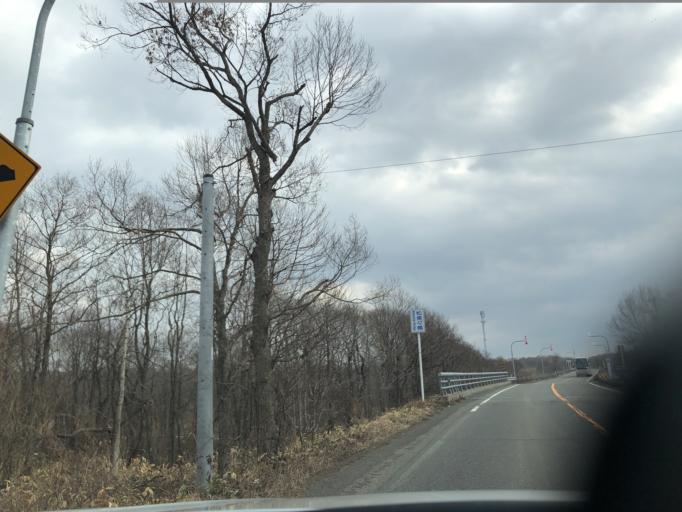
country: JP
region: Hokkaido
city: Chitose
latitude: 42.7660
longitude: 141.7183
